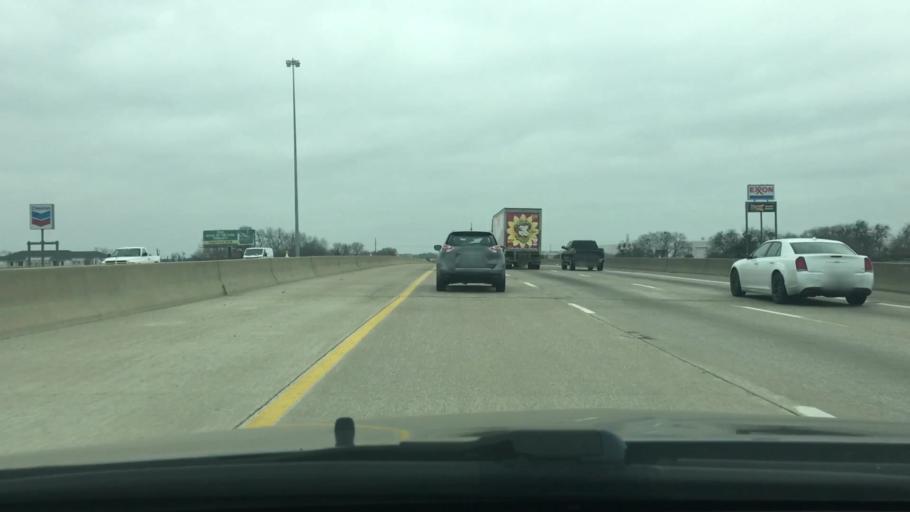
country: US
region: Texas
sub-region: Dallas County
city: Wilmer
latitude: 32.5918
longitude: -96.6795
